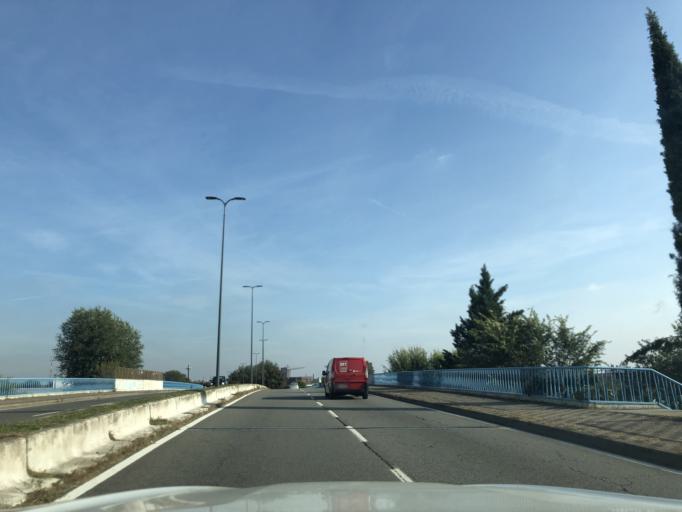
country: IT
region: Lombardy
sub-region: Citta metropolitana di Milano
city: Novate Milanese
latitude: 45.5126
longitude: 9.1601
